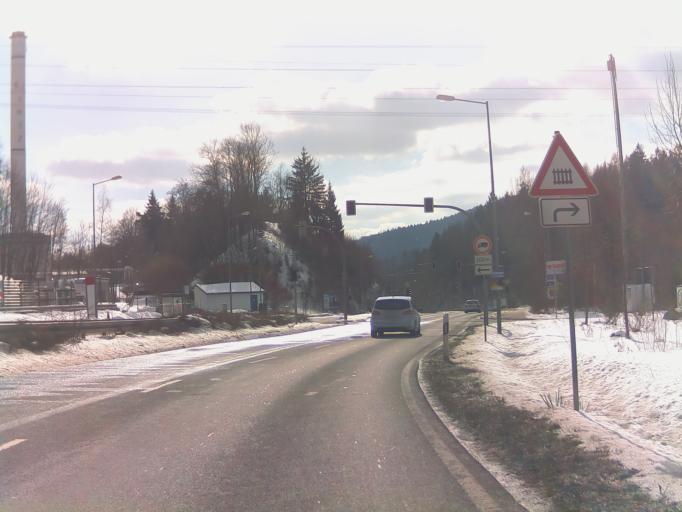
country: DE
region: Thuringia
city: Suhl
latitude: 50.6342
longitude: 10.6980
